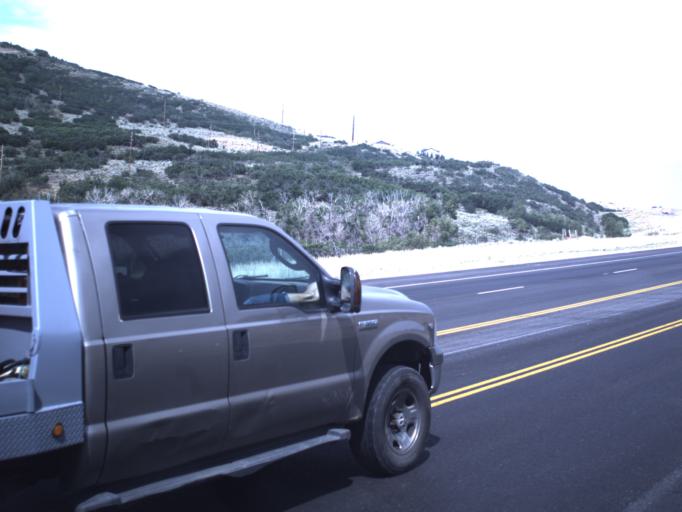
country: US
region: Utah
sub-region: Summit County
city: Park City
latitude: 40.6657
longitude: -111.4186
